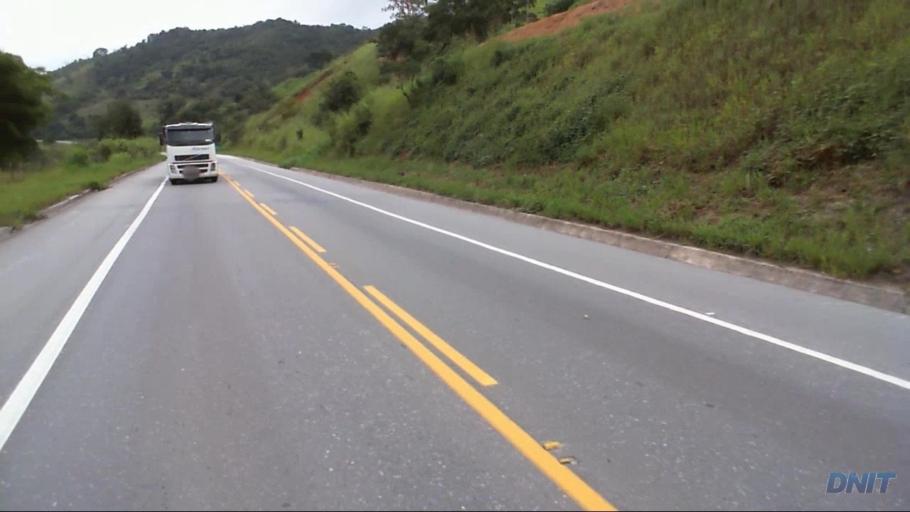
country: BR
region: Minas Gerais
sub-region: Nova Era
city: Nova Era
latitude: -19.7177
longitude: -43.0028
